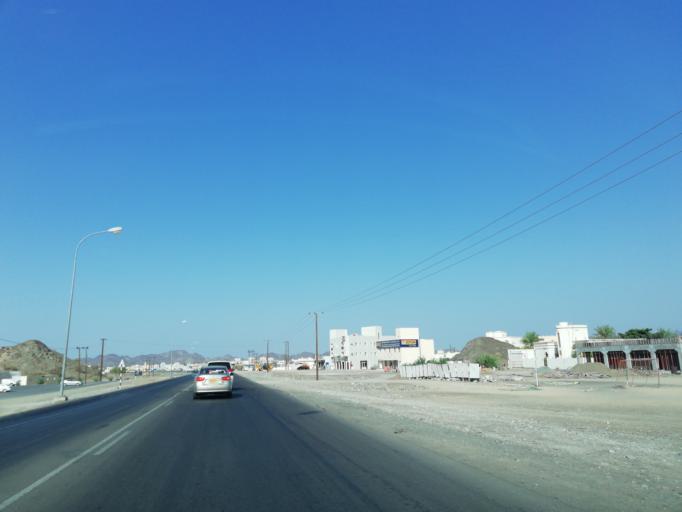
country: OM
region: Ash Sharqiyah
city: Ibra'
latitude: 22.7946
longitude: 58.1520
